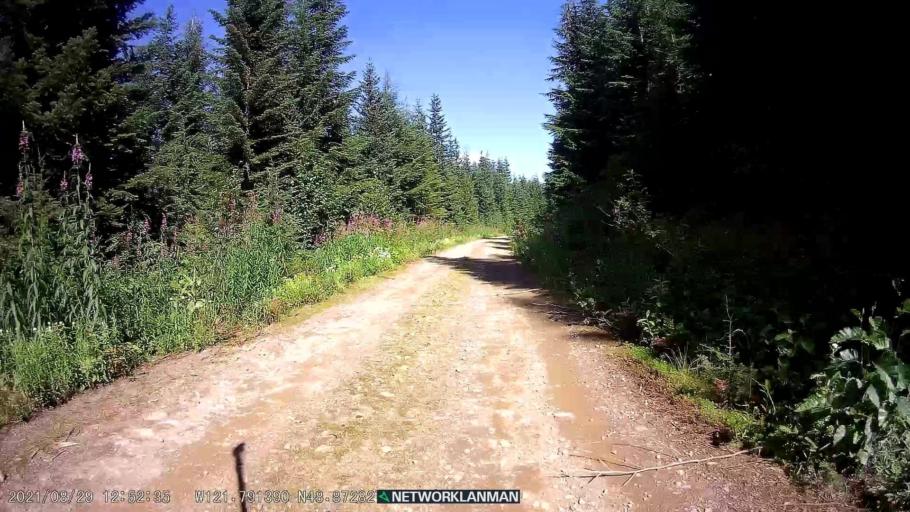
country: CA
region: British Columbia
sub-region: Fraser Valley Regional District
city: Chilliwack
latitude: 48.8727
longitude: -121.7916
